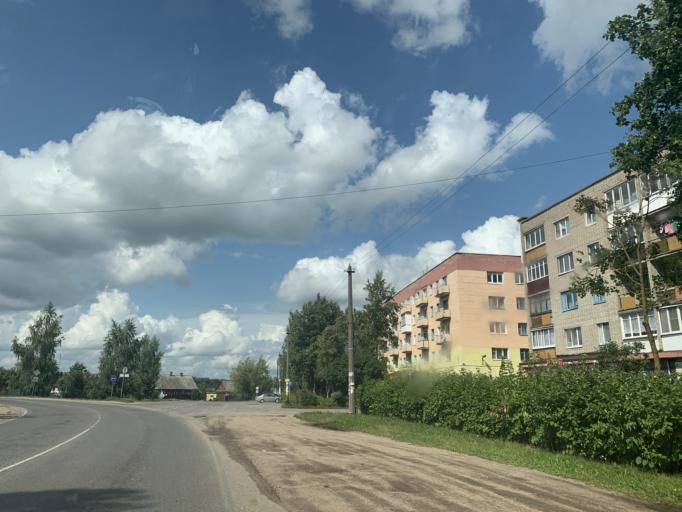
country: BY
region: Minsk
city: Enyerhyetykaw
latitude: 53.5869
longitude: 27.0527
